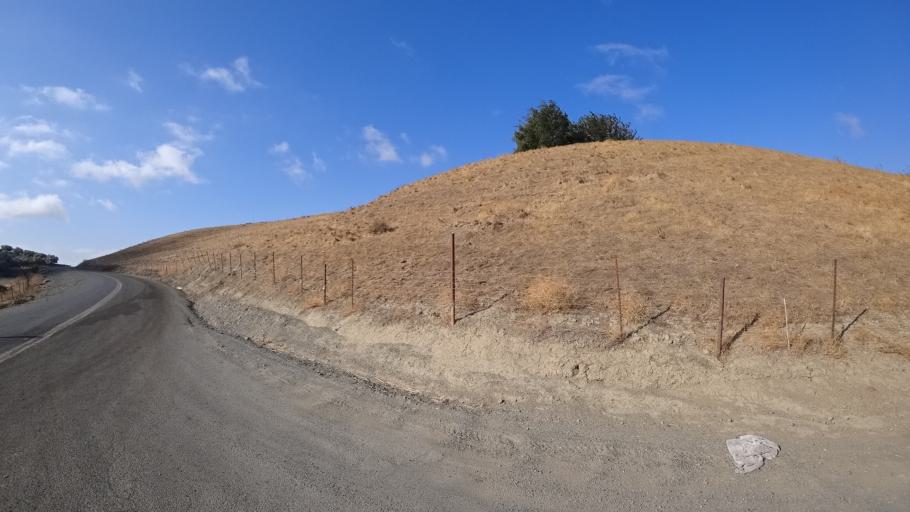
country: US
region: California
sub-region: Yolo County
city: Dunnigan
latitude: 38.8034
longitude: -122.0064
